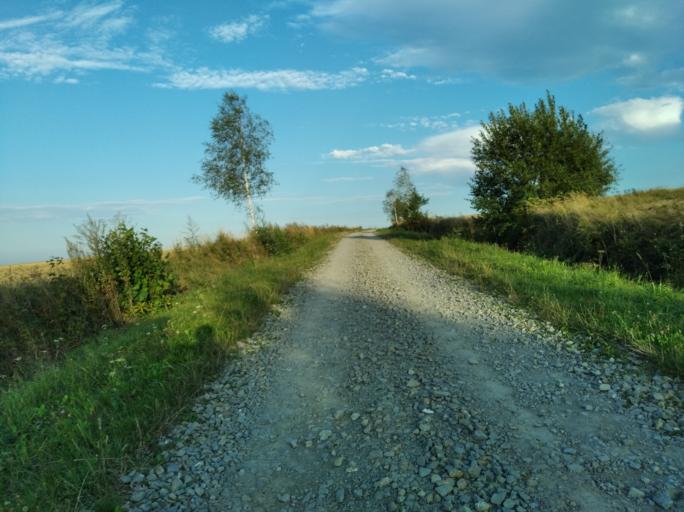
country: PL
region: Subcarpathian Voivodeship
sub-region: Powiat ropczycko-sedziszowski
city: Wielopole Skrzynskie
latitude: 49.9136
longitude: 21.5956
